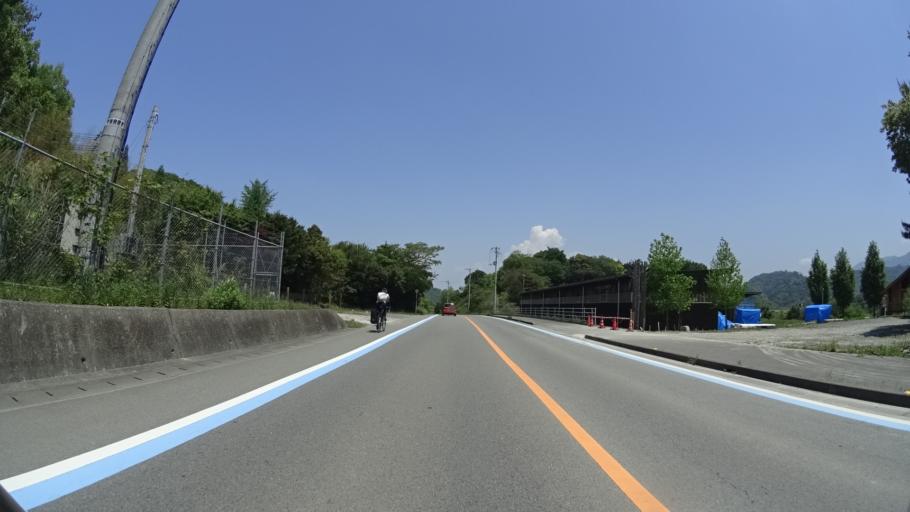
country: JP
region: Ehime
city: Iyo
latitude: 33.7188
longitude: 132.6768
